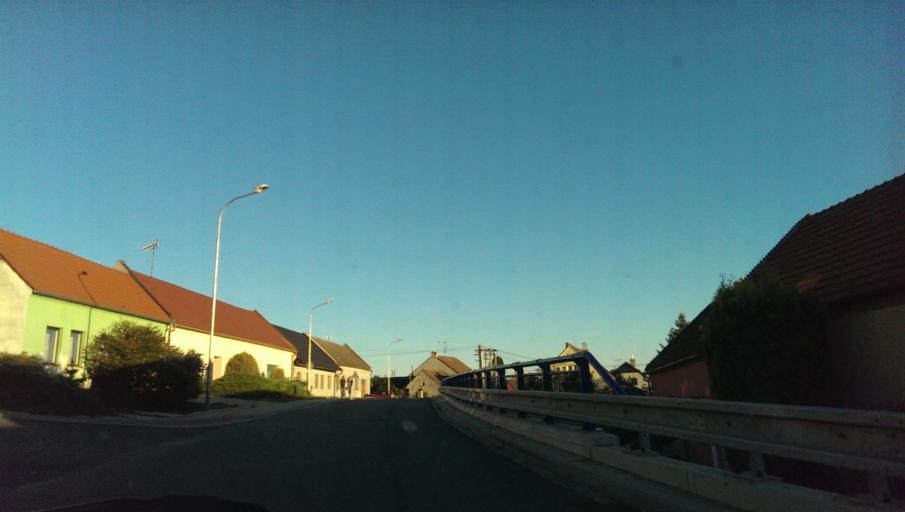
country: CZ
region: Zlin
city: Tupesy
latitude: 49.0839
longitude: 17.3735
